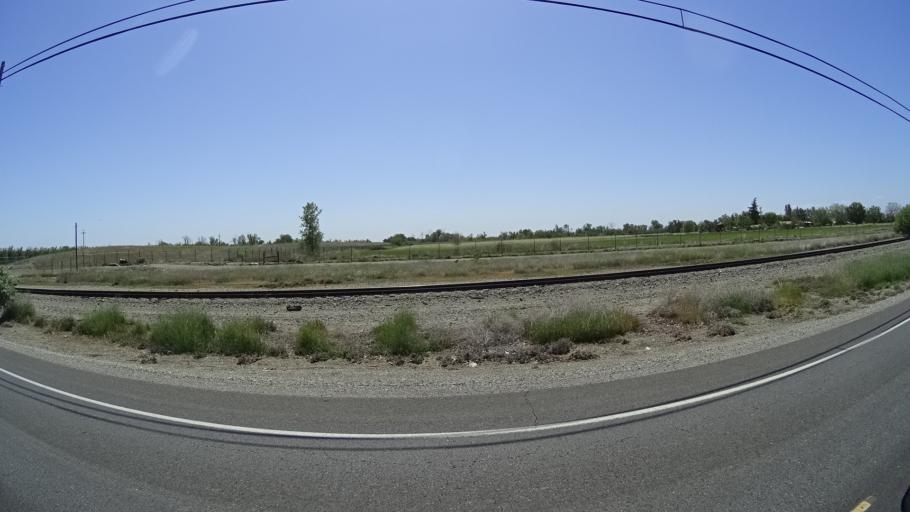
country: US
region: California
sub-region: Glenn County
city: Orland
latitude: 39.7690
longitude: -122.1567
